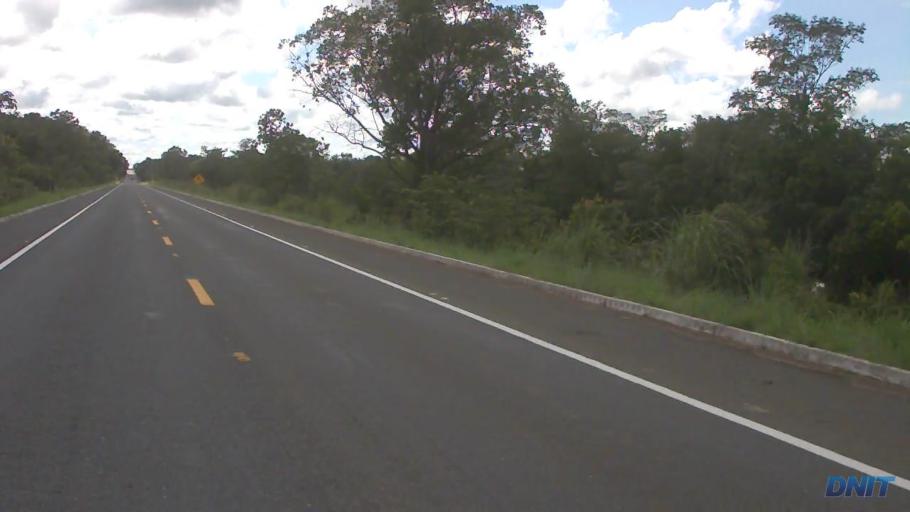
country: BR
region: Goias
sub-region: Sao Miguel Do Araguaia
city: Sao Miguel do Araguaia
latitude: -13.2858
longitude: -50.4803
